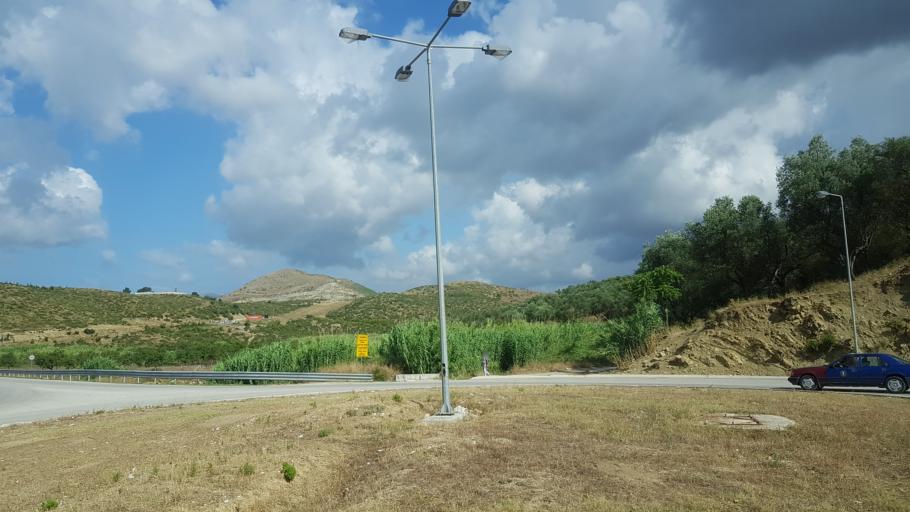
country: AL
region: Vlore
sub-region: Rrethi i Delvines
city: Mesopotam
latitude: 39.9008
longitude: 20.0845
